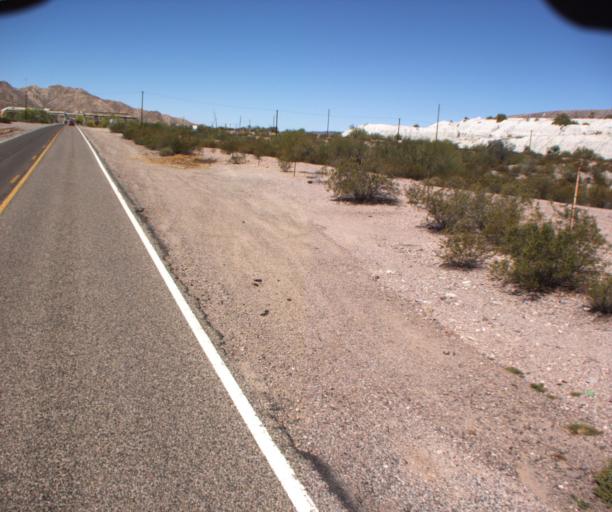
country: US
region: Arizona
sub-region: Pima County
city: Ajo
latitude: 32.3688
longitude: -112.8487
